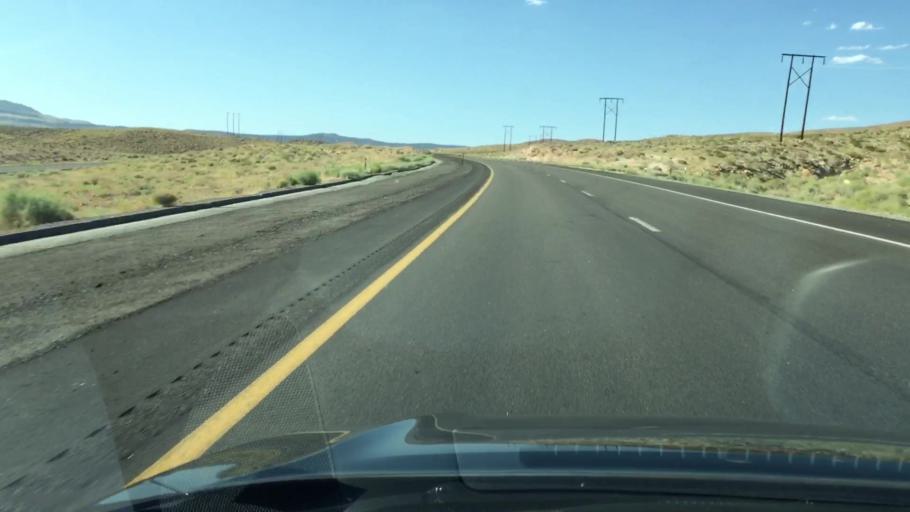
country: US
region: California
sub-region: Inyo County
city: West Bishop
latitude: 37.4510
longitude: -118.5725
